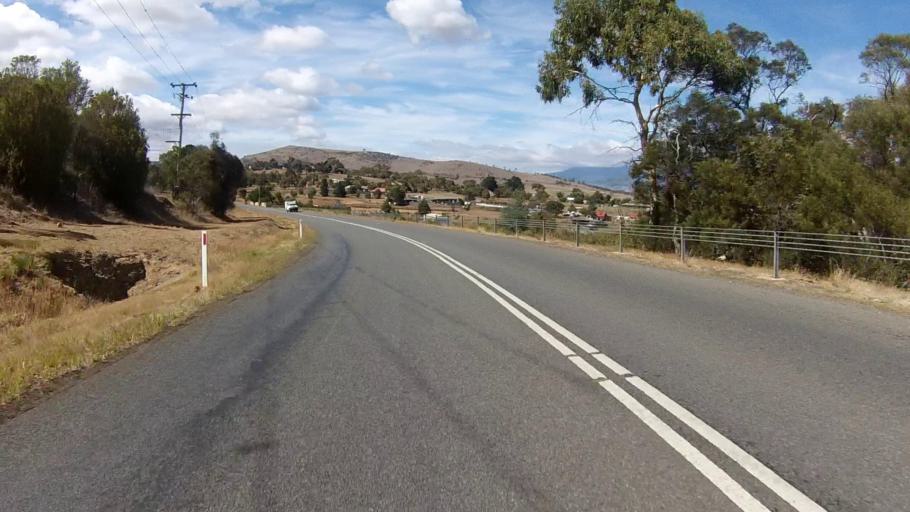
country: AU
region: Tasmania
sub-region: Brighton
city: Bridgewater
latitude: -42.7093
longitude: 147.2691
